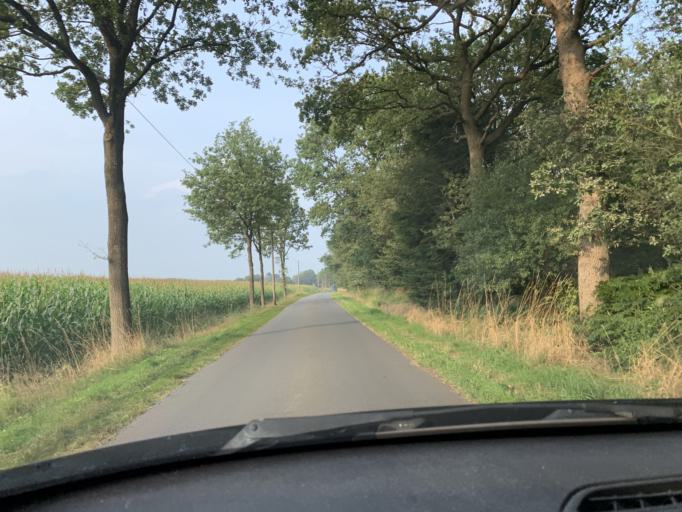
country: DE
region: Lower Saxony
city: Apen
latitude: 53.2539
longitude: 7.8407
